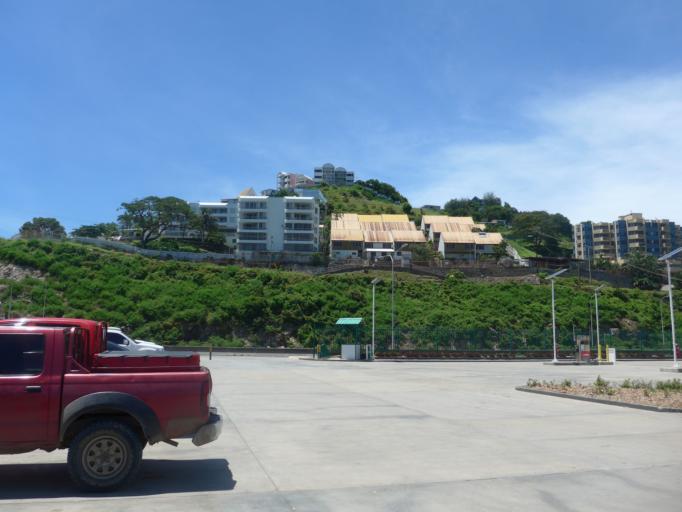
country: PG
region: National Capital
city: Port Moresby
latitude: -9.4818
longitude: 147.1671
